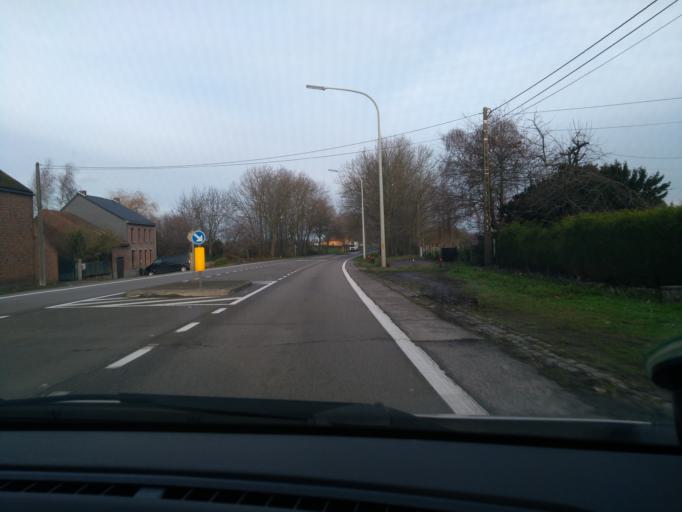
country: BE
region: Wallonia
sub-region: Province du Hainaut
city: Quevy-le-Petit
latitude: 50.3564
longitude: 3.9672
